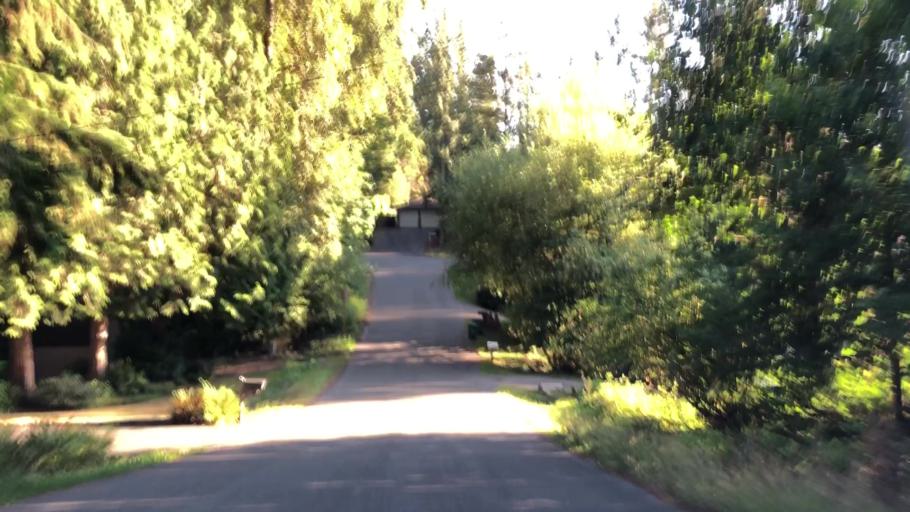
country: US
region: Washington
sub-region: King County
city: Cottage Lake
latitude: 47.7400
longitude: -122.0958
